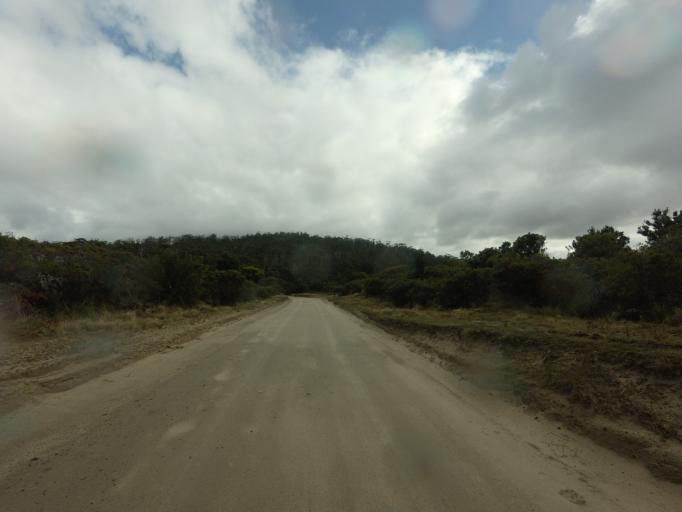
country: AU
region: Tasmania
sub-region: Huon Valley
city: Geeveston
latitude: -43.5804
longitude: 146.8882
